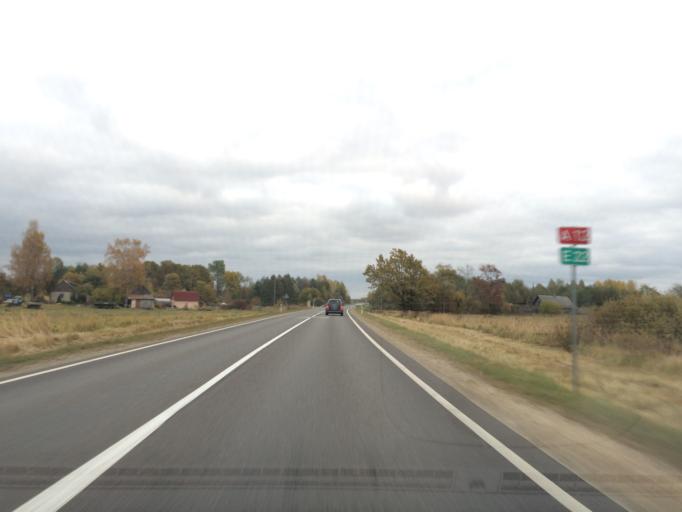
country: LV
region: Livani
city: Livani
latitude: 56.5322
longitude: 26.2342
